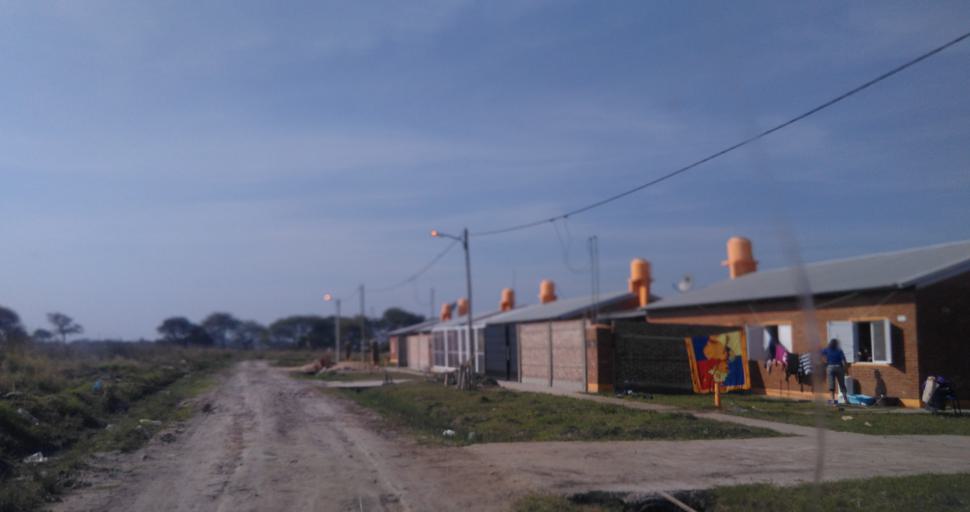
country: AR
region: Chaco
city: Fontana
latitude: -27.4545
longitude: -59.0477
